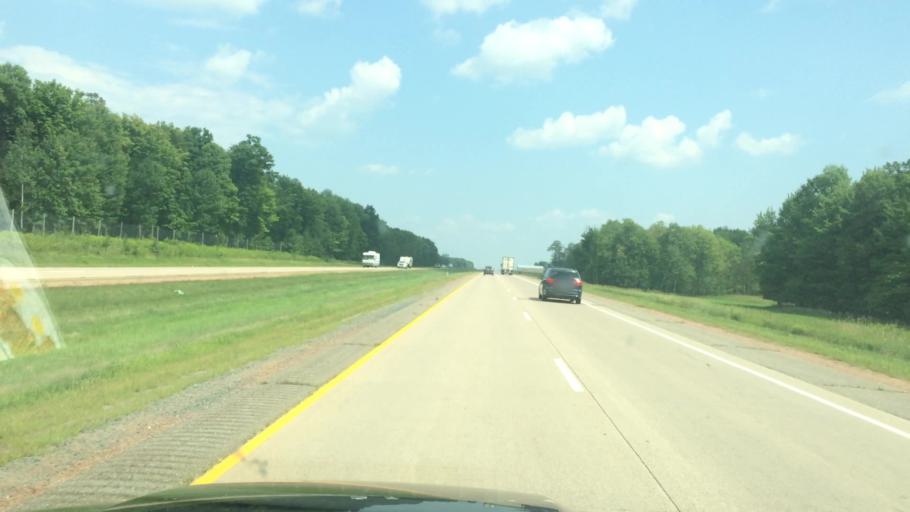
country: US
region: Wisconsin
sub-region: Marathon County
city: Athens
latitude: 44.9452
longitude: -90.1533
